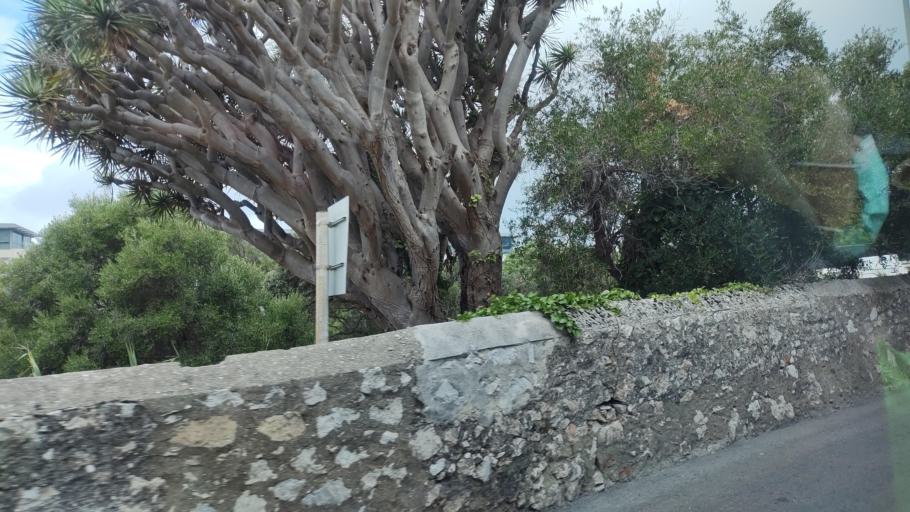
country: GI
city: Gibraltar
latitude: 36.1182
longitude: -5.3482
